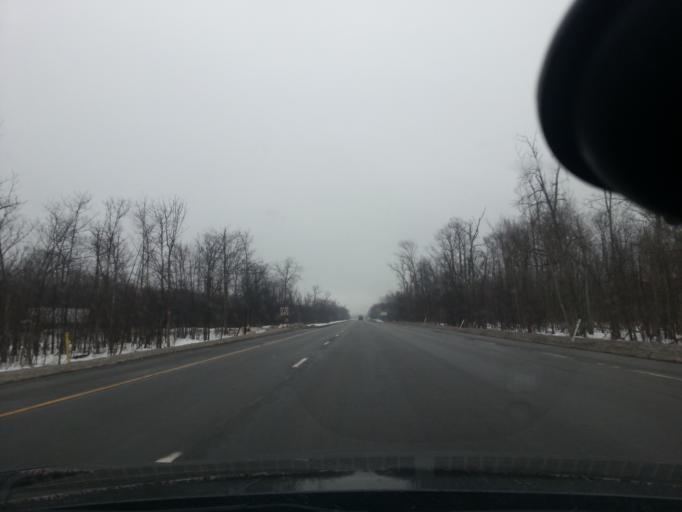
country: US
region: New York
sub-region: Jefferson County
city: Adams
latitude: 43.7208
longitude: -76.0770
